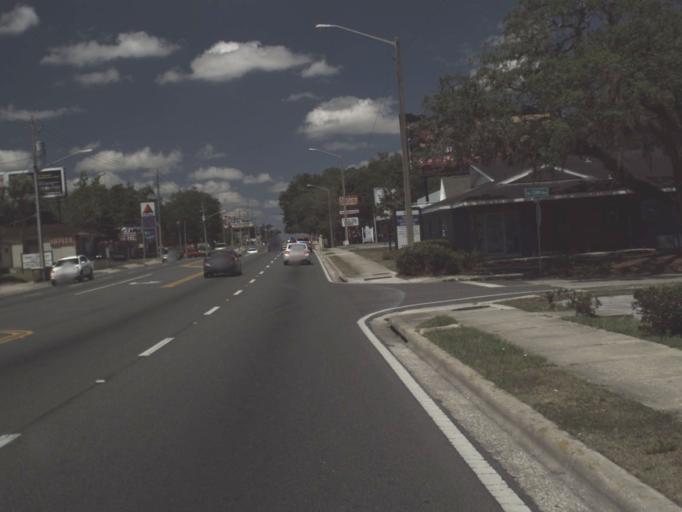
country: US
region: Florida
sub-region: Marion County
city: Ocala
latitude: 29.1871
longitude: -82.1208
